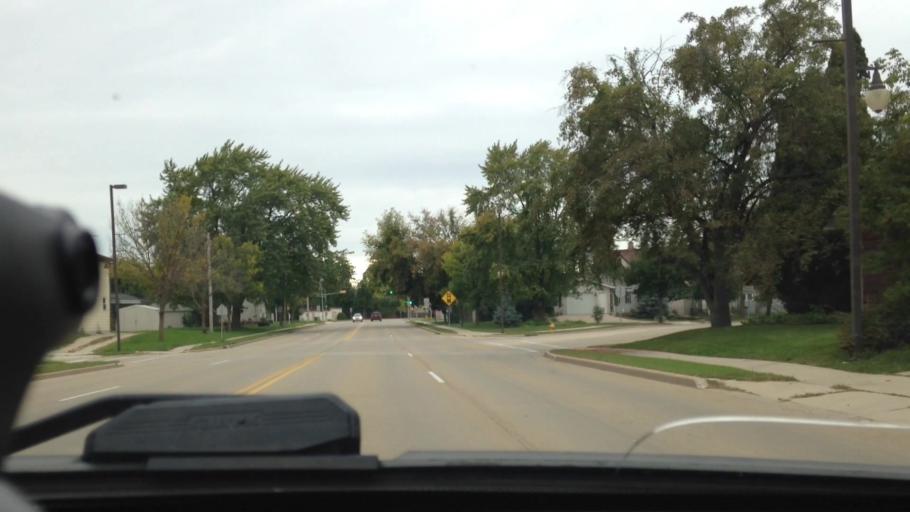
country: US
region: Wisconsin
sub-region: Fond du Lac County
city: North Fond du Lac
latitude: 43.8050
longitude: -88.4821
